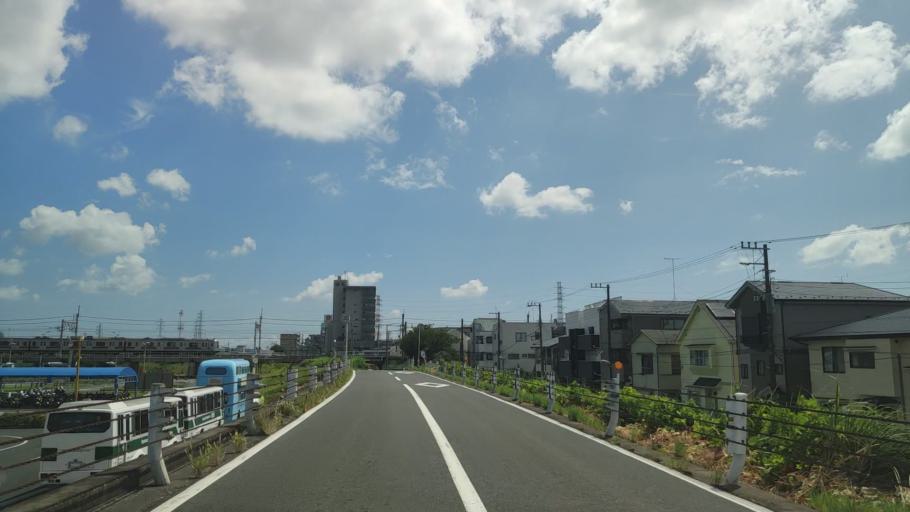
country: JP
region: Kanagawa
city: Yokohama
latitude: 35.5329
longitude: 139.6320
